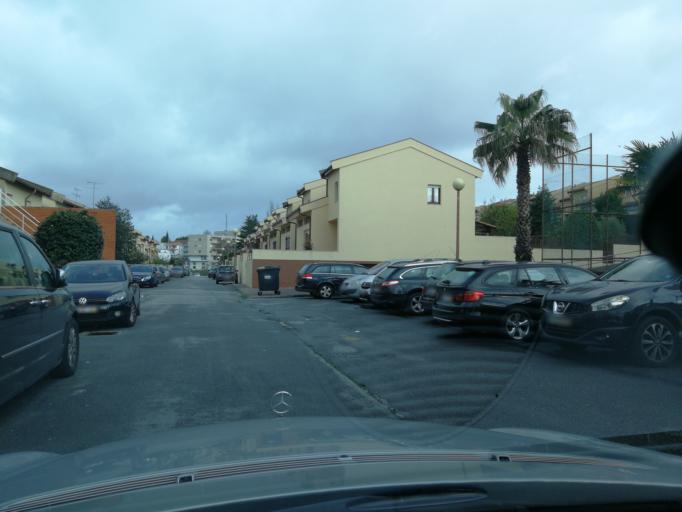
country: PT
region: Braga
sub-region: Braga
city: Braga
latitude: 41.5320
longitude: -8.4149
